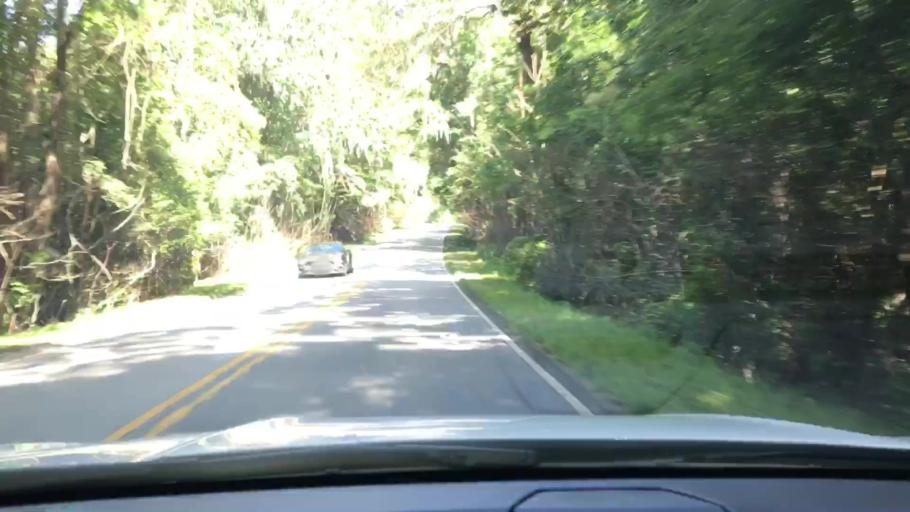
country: US
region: South Carolina
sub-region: Berkeley County
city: Ladson
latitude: 32.8972
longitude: -80.1377
